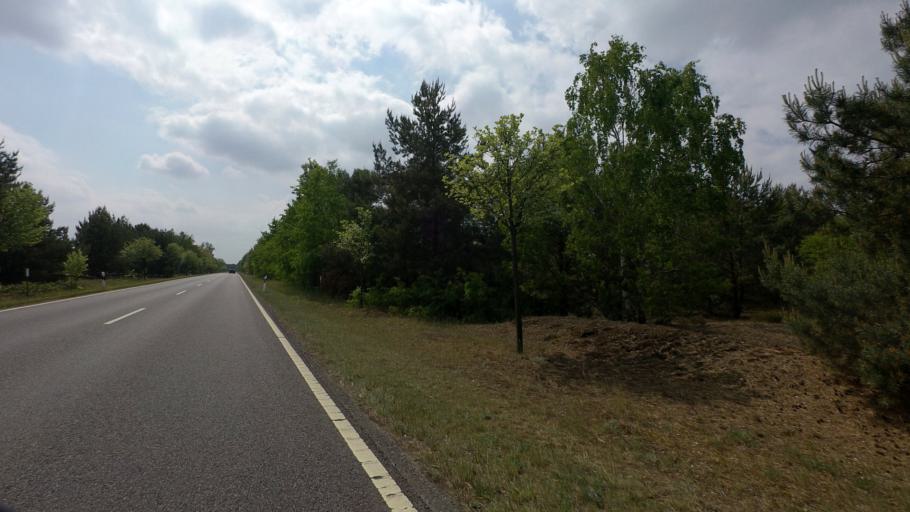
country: DE
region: Brandenburg
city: Drachhausen
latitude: 51.9417
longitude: 14.3390
